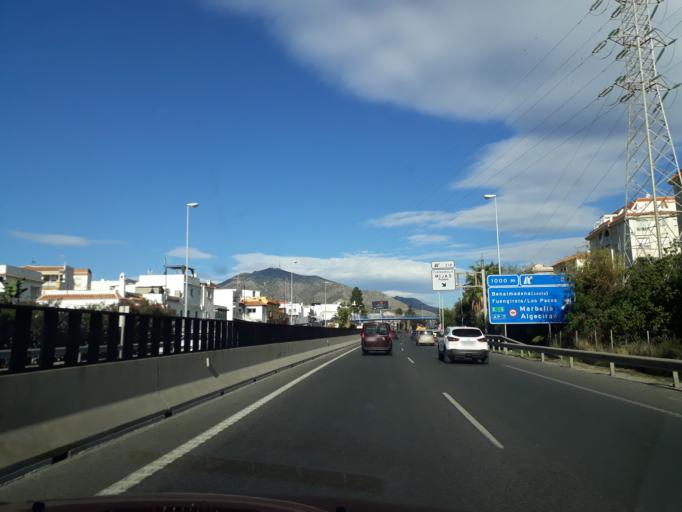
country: ES
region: Andalusia
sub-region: Provincia de Malaga
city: Fuengirola
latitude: 36.5481
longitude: -4.6309
